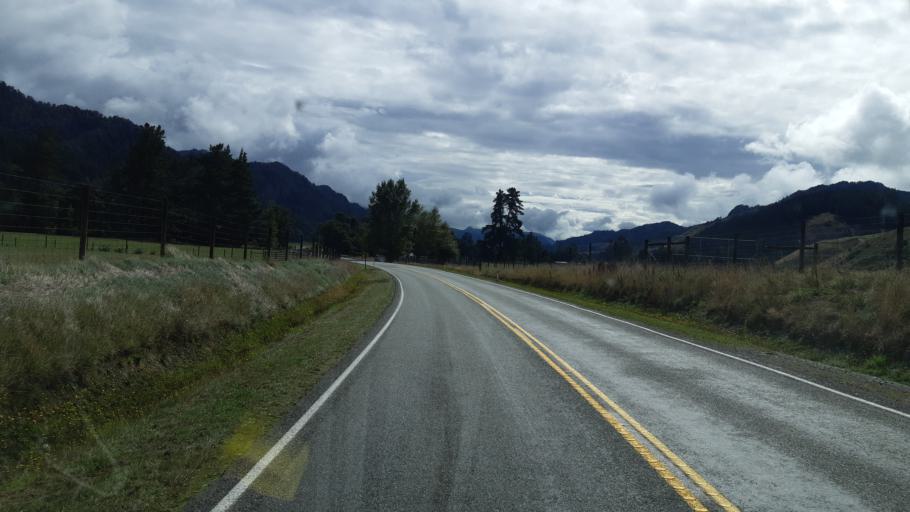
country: NZ
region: Tasman
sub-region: Tasman District
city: Wakefield
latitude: -41.7767
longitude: 172.3776
